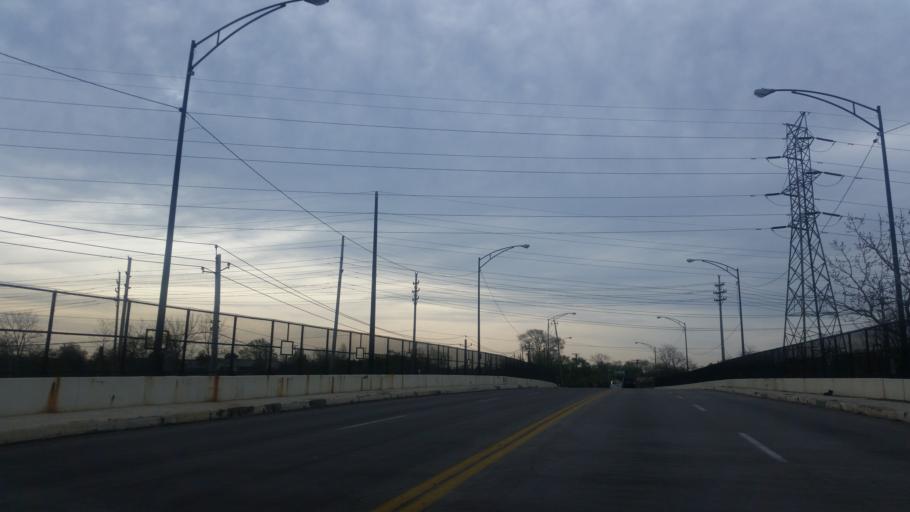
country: US
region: Ohio
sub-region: Cuyahoga County
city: Newburgh Heights
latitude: 41.4738
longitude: -81.6267
